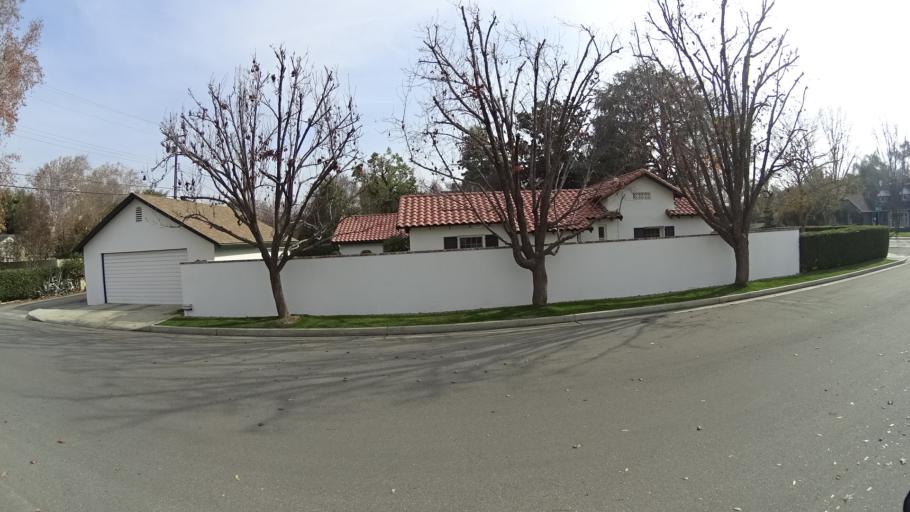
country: US
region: California
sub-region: Kern County
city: Bakersfield
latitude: 35.3786
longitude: -119.0329
